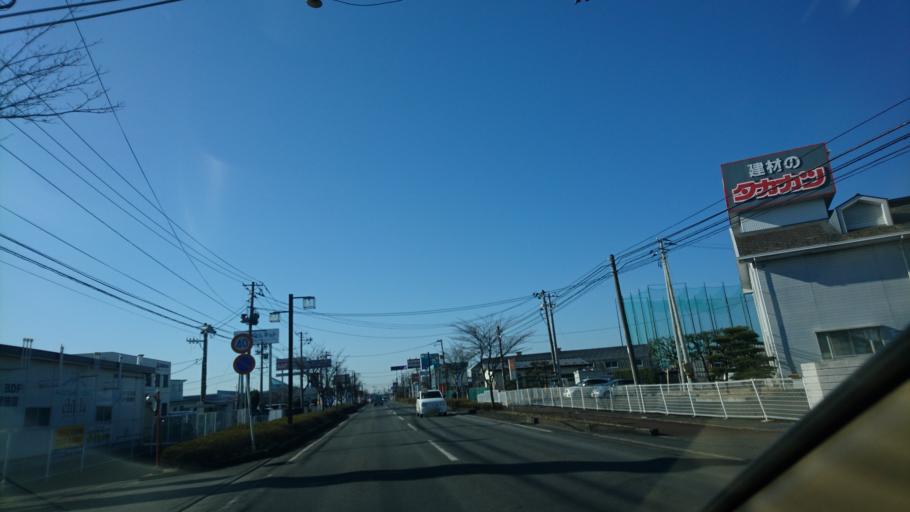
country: JP
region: Miyagi
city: Furukawa
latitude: 38.6017
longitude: 140.9789
